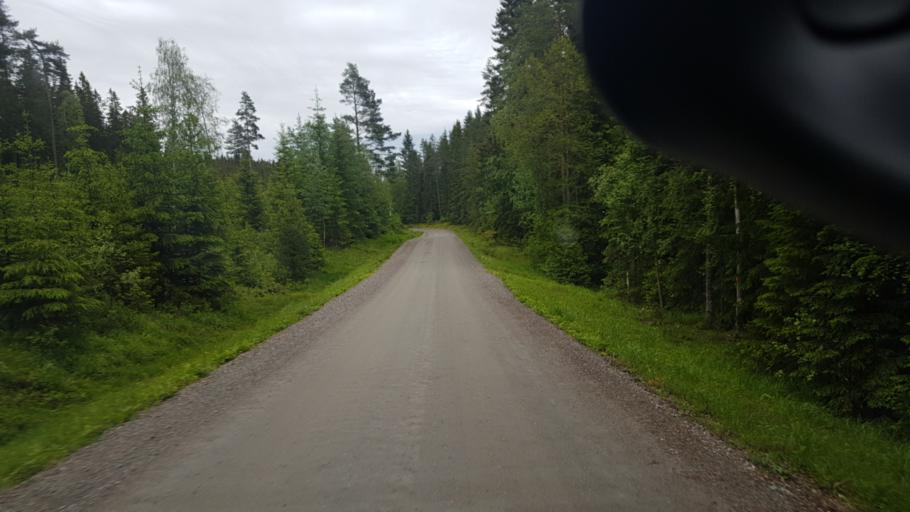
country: NO
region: Ostfold
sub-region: Romskog
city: Romskog
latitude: 59.7111
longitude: 12.0317
